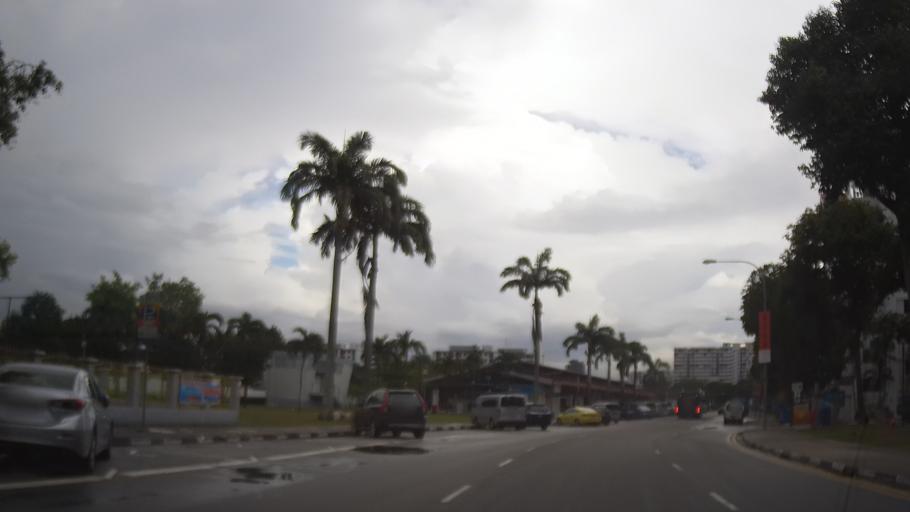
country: SG
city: Singapore
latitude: 1.3242
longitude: 103.8850
